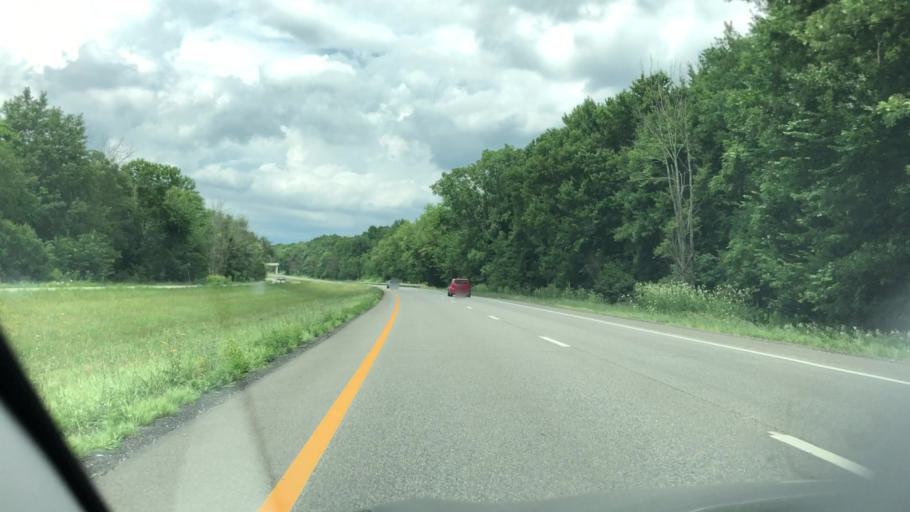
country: US
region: Ohio
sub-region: Summit County
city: Norton
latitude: 41.0643
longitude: -81.6620
